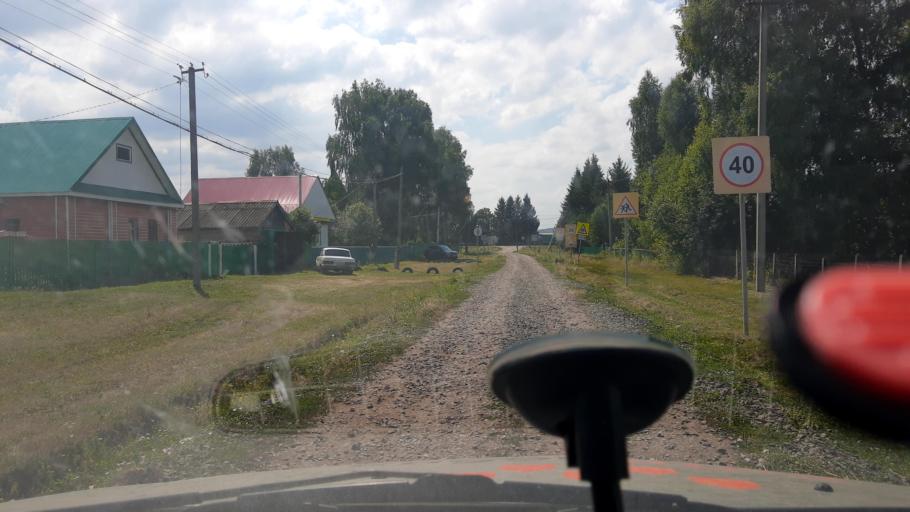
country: RU
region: Bashkortostan
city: Chekmagush
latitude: 54.8775
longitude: 54.6147
